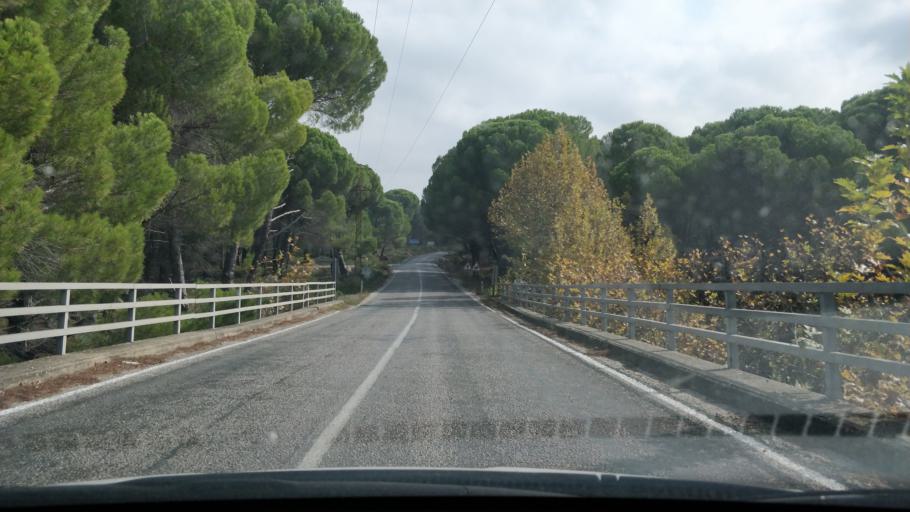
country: TR
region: Balikesir
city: Altinova
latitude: 39.2666
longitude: 26.9055
